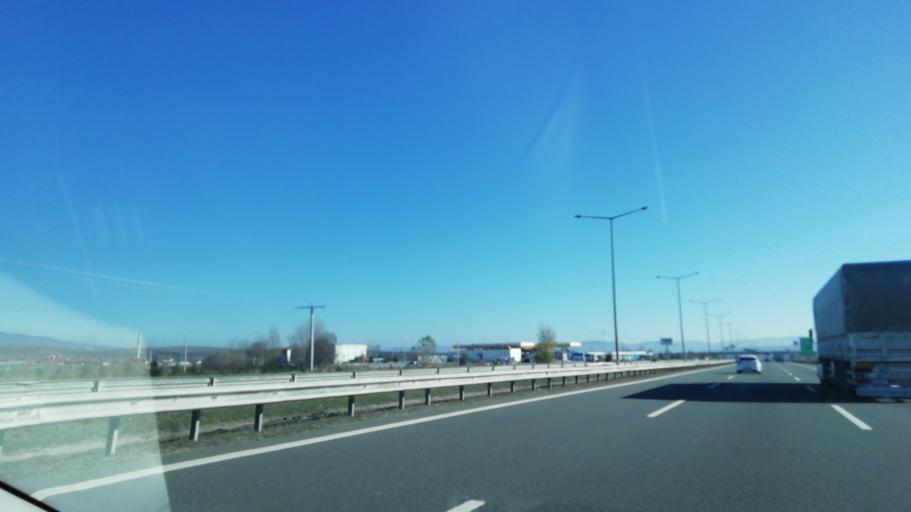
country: TR
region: Bolu
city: Dortdivan
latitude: 40.7539
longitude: 32.0729
